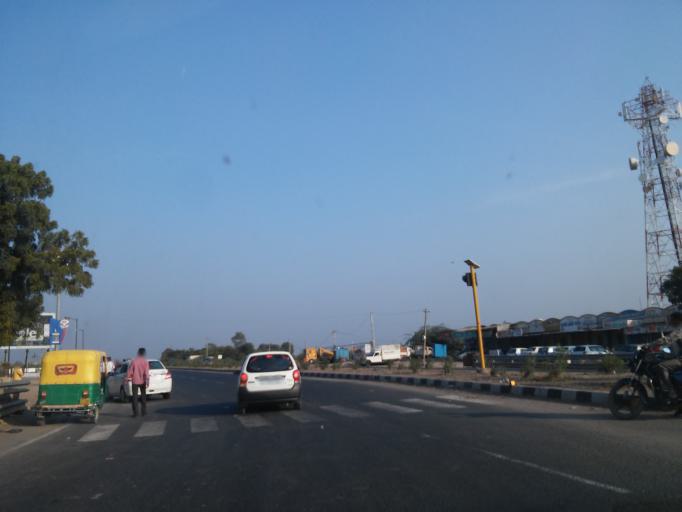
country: IN
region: Gujarat
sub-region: Ahmadabad
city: Mandal
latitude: 23.0980
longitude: 72.0631
